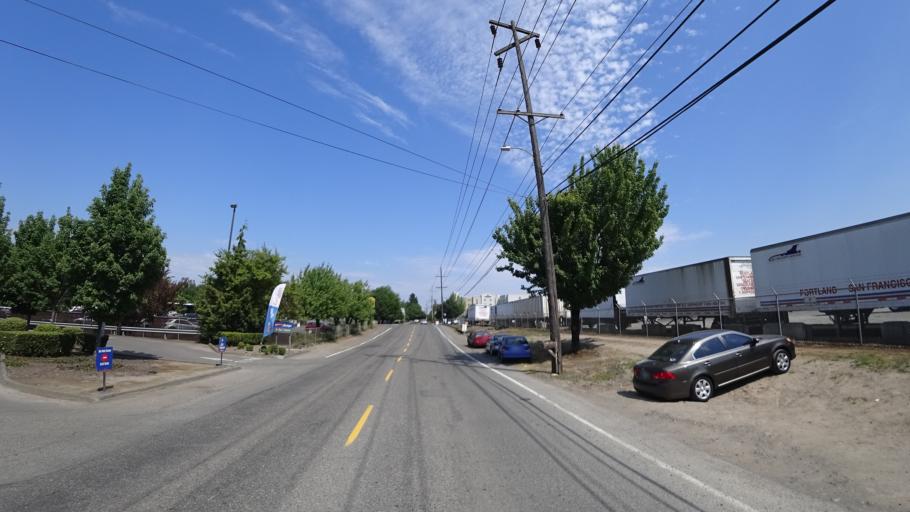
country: US
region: Oregon
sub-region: Multnomah County
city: Lents
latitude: 45.5682
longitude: -122.5495
